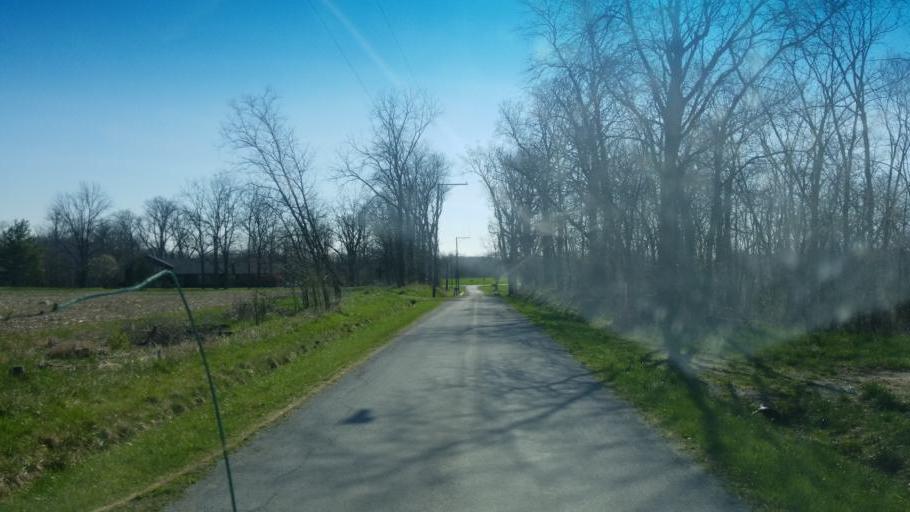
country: US
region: Ohio
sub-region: Hardin County
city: Forest
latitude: 40.7094
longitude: -83.4480
